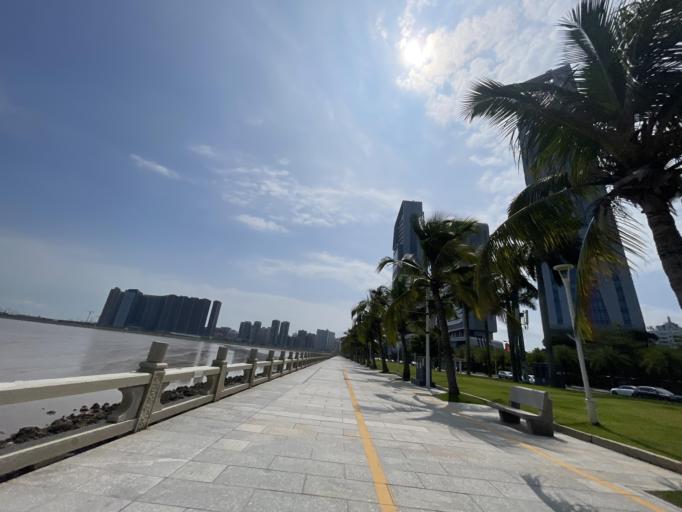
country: MO
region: Macau
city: Macau
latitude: 22.2243
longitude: 113.5559
